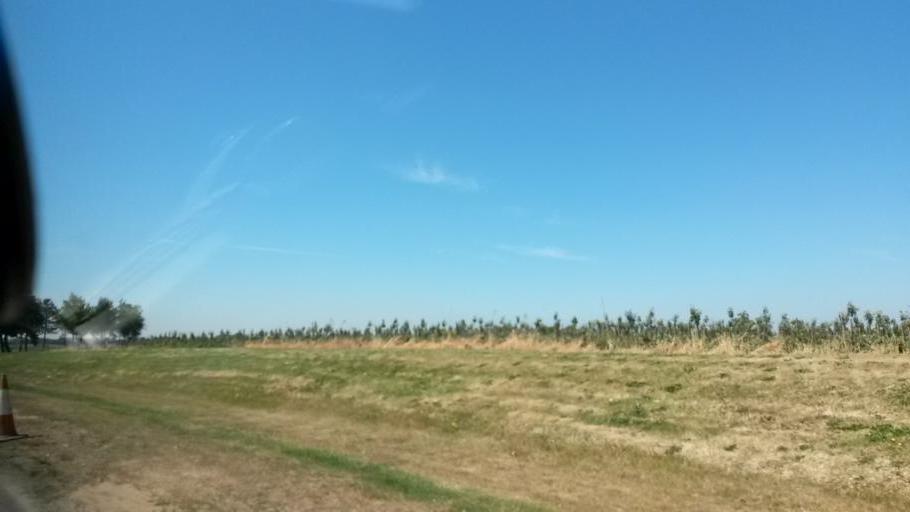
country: IE
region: Leinster
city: Ballymun
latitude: 53.4405
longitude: -6.2840
